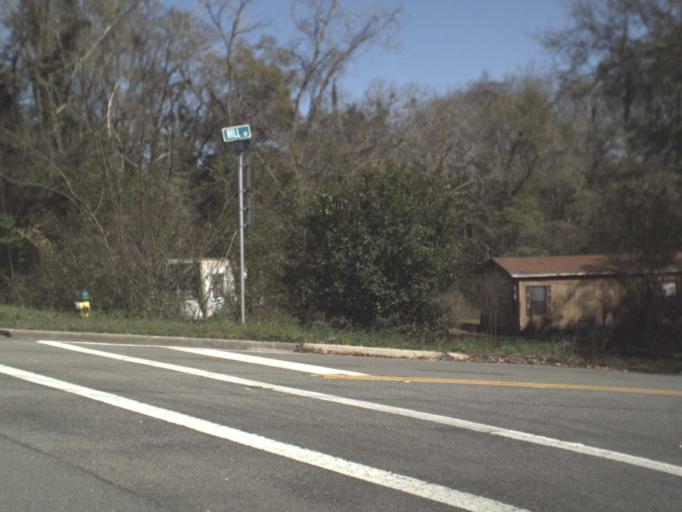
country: US
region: Florida
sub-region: Leon County
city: Tallahassee
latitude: 30.4192
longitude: -84.2310
